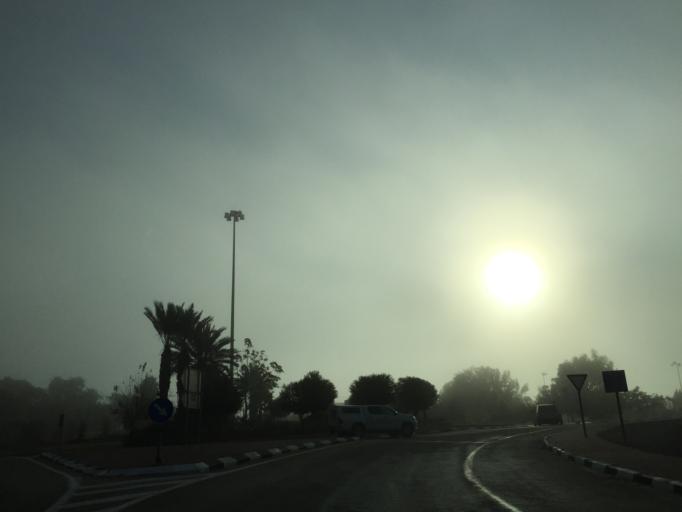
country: IL
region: Southern District
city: Yeroham
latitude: 30.9902
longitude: 34.9109
